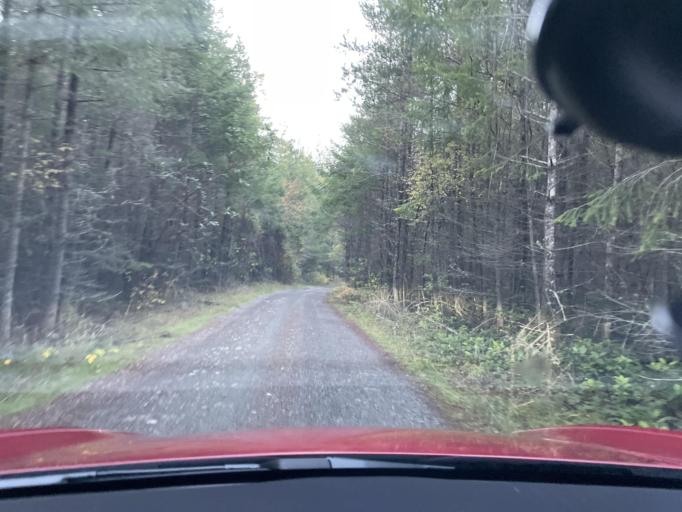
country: US
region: Washington
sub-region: San Juan County
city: Friday Harbor
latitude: 48.6161
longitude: -123.1400
